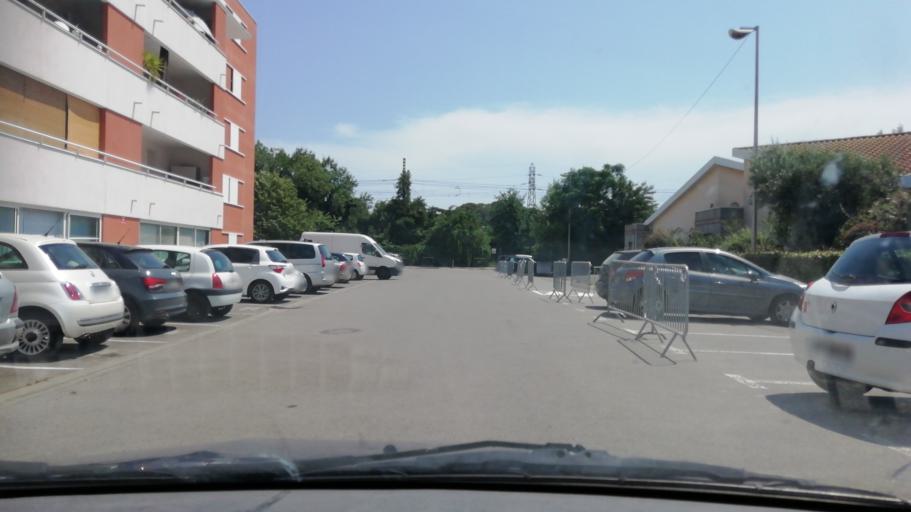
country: FR
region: Languedoc-Roussillon
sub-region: Departement de l'Herault
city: Castelnau-le-Lez
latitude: 43.6275
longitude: 3.8996
